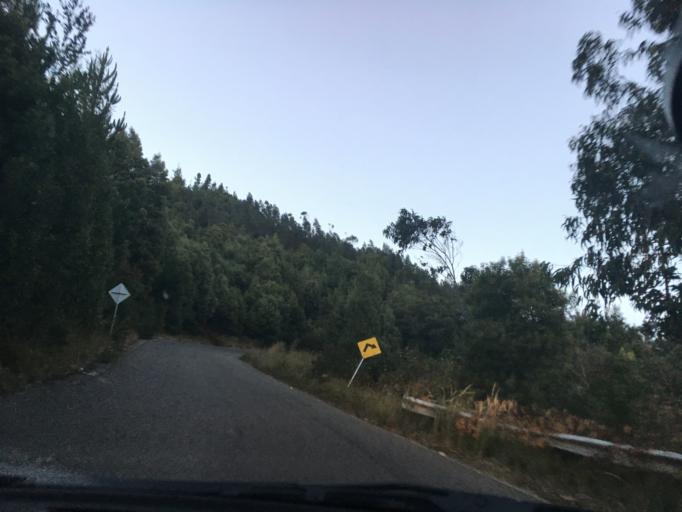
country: CO
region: Boyaca
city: Aquitania
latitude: 5.6132
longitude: -72.9099
